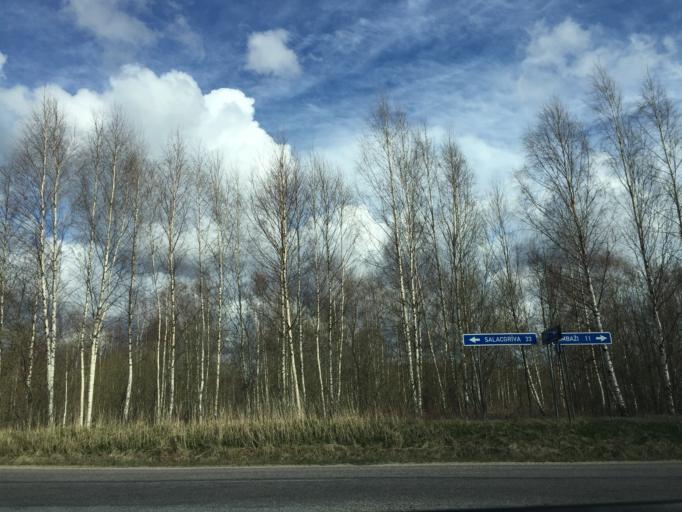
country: LV
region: Limbazu Rajons
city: Limbazi
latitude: 57.6091
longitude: 24.6561
